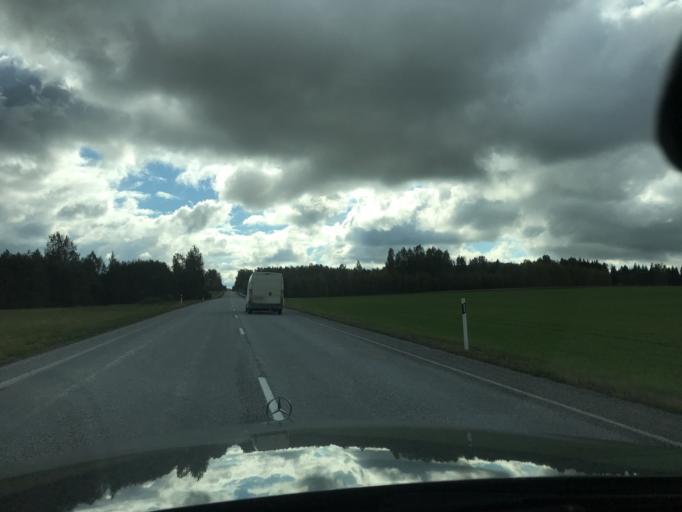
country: RU
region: Pskov
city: Pechory
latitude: 57.7187
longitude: 27.3178
